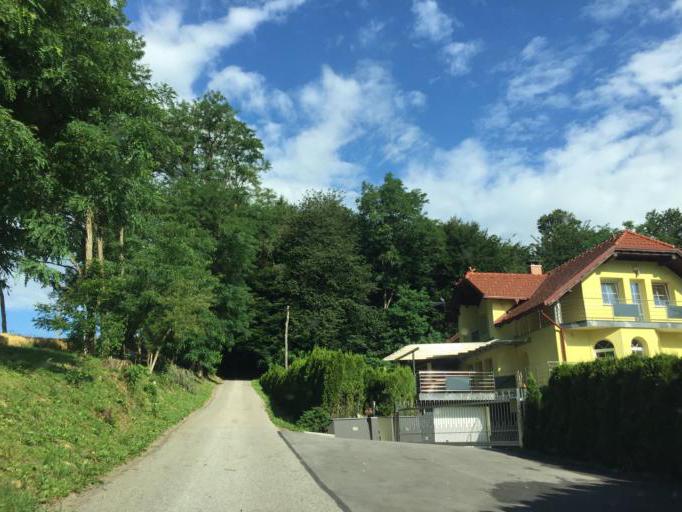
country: SI
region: Gornja Radgona
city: Gornja Radgona
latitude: 46.6731
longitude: 15.9680
